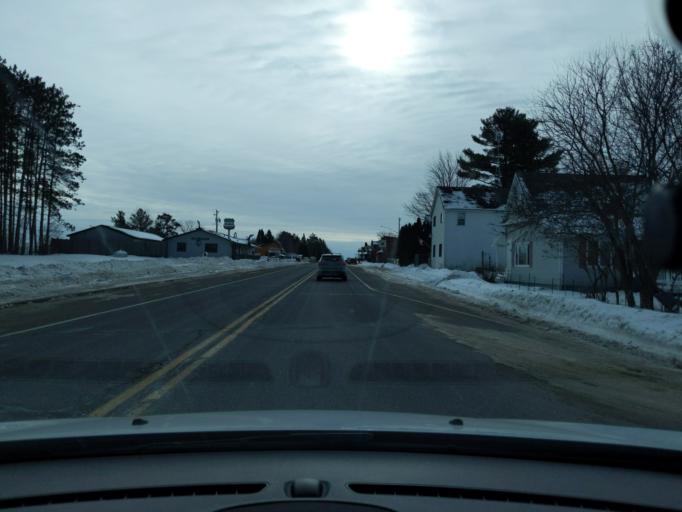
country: US
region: Wisconsin
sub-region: Barron County
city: Cumberland
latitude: 45.6380
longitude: -91.9927
